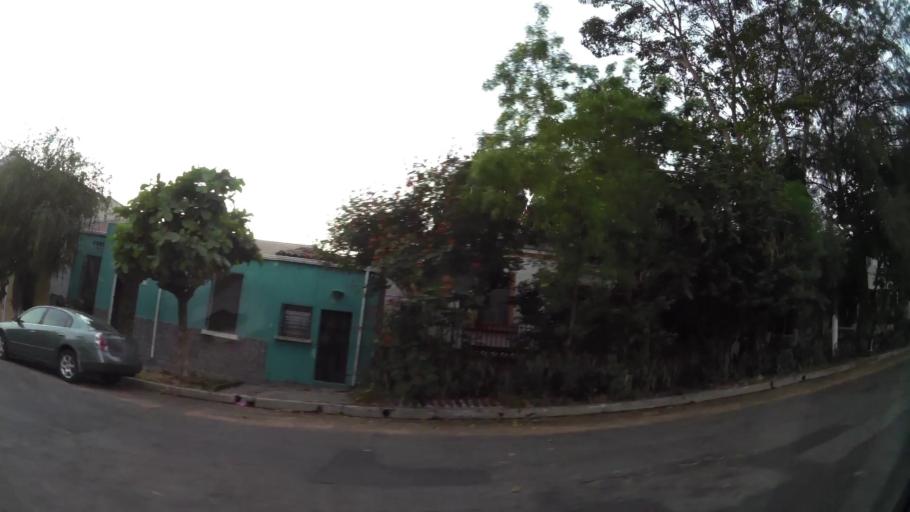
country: SV
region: San Salvador
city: San Salvador
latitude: 13.7062
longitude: -89.1836
